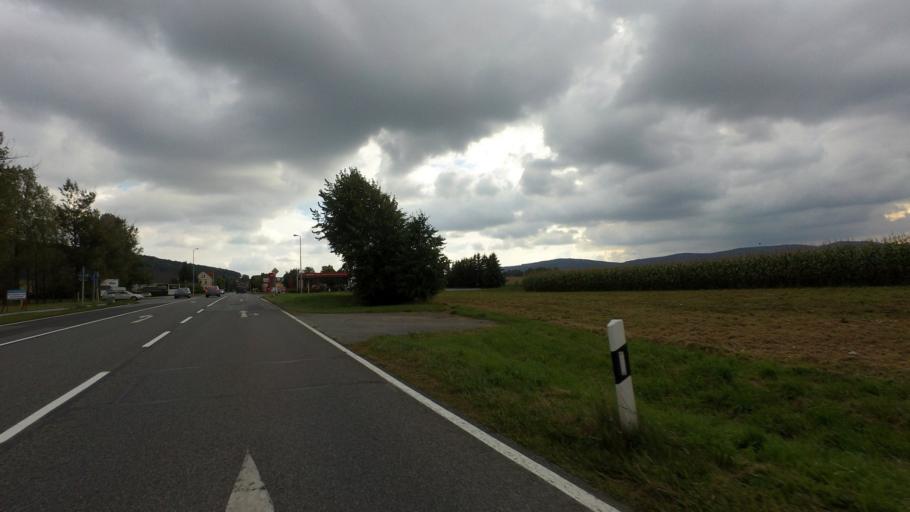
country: DE
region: Saxony
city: Grosspostwitz
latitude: 51.1446
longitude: 14.4401
